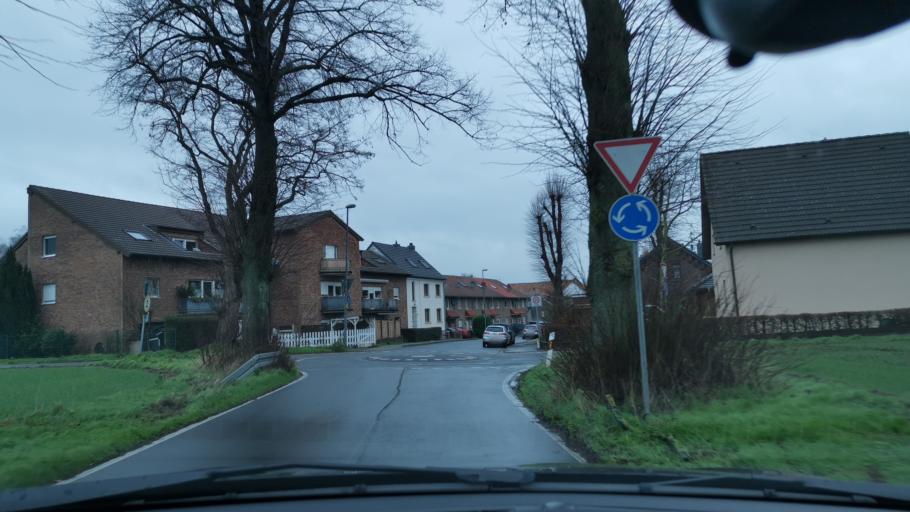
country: DE
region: North Rhine-Westphalia
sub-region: Regierungsbezirk Koln
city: Bedburg
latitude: 50.9945
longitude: 6.5110
